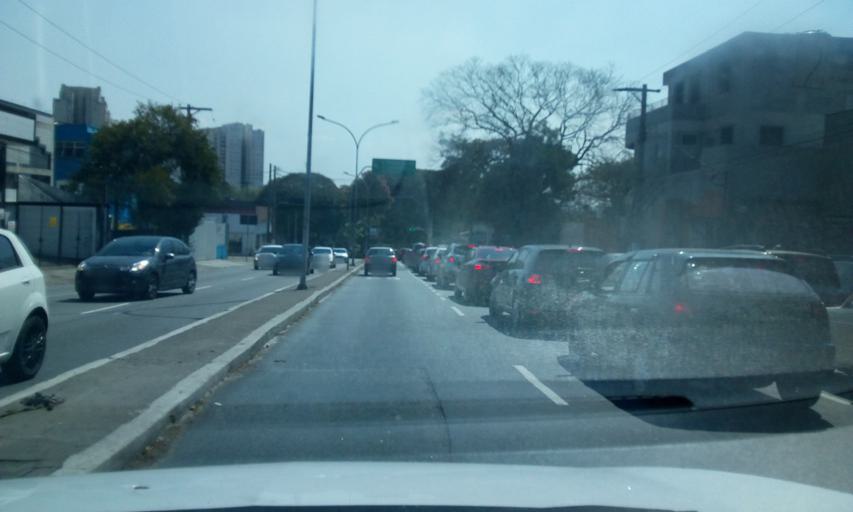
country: BR
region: Sao Paulo
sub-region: Osasco
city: Osasco
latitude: -23.5211
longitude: -46.7199
